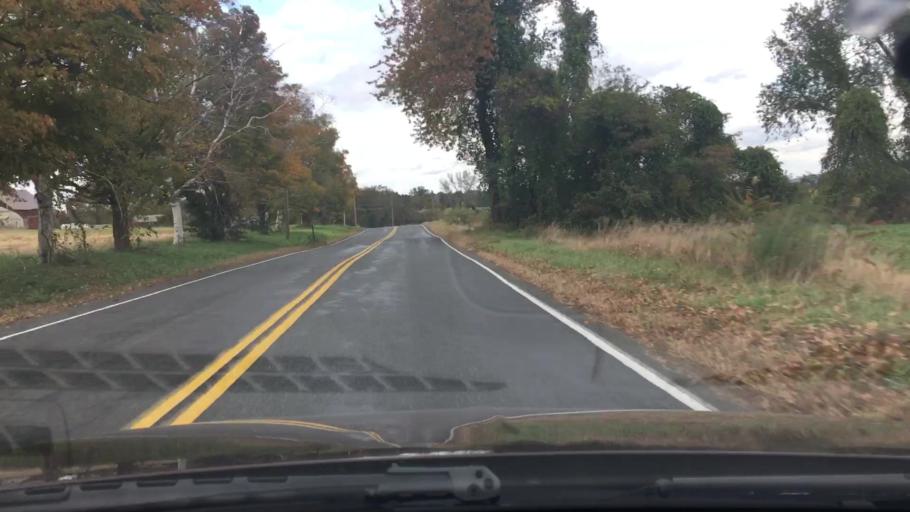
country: US
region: Connecticut
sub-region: Tolland County
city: Somers
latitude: 41.9568
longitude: -72.4826
